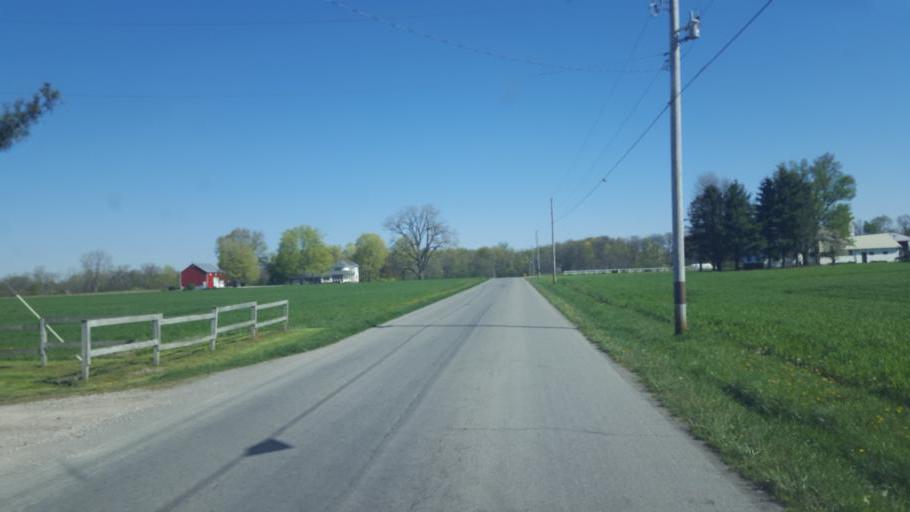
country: US
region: Ohio
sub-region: Wyandot County
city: Upper Sandusky
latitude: 40.8856
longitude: -83.2228
